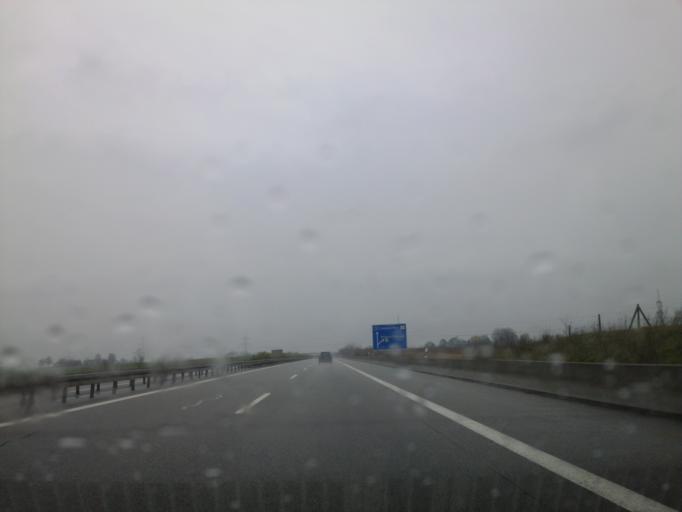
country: DE
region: Mecklenburg-Vorpommern
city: Papendorf
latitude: 54.0214
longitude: 12.1110
